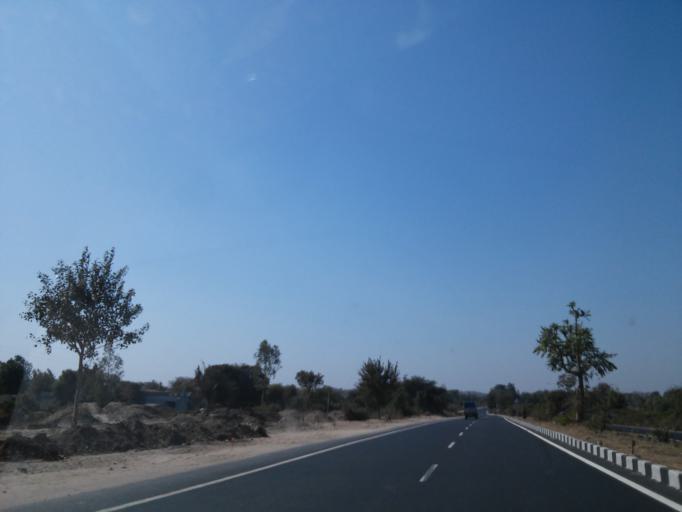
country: IN
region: Gujarat
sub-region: Sabar Kantha
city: Himatnagar
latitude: 23.5983
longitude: 73.1531
